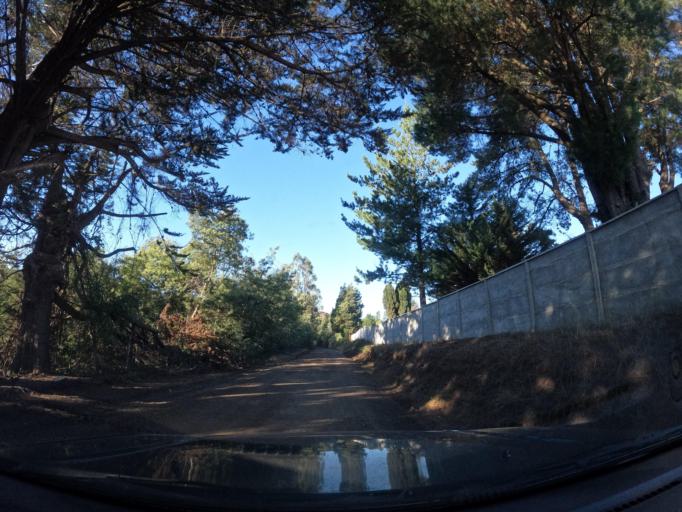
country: CL
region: Biobio
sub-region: Provincia de Concepcion
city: Chiguayante
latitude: -37.0296
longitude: -72.8746
